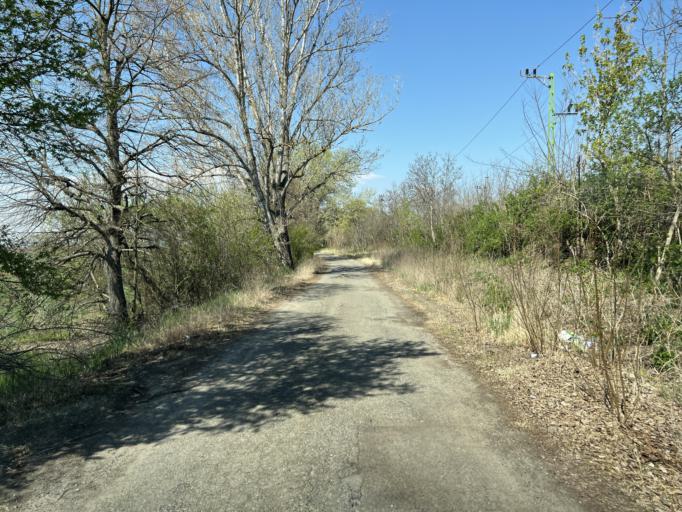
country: HU
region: Pest
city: Szod
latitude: 47.7324
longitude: 19.2200
